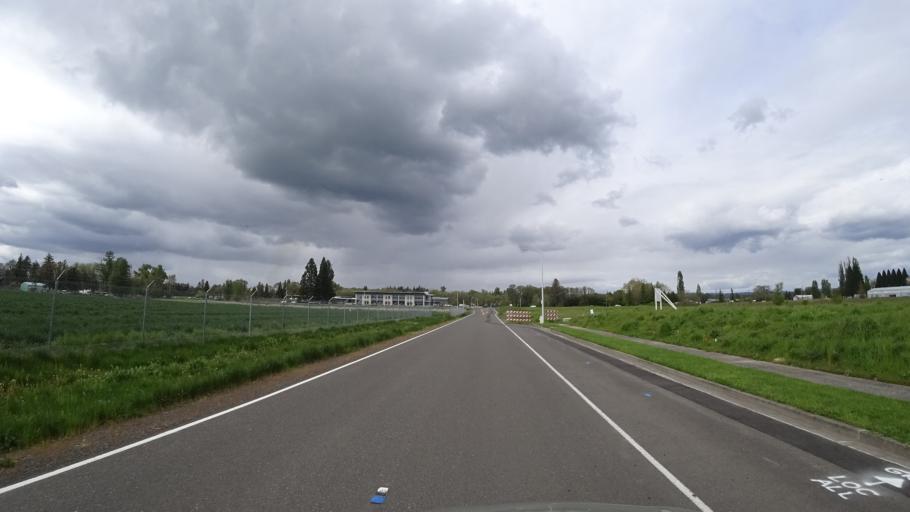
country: US
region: Oregon
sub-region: Washington County
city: Hillsboro
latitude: 45.5490
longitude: -122.9483
